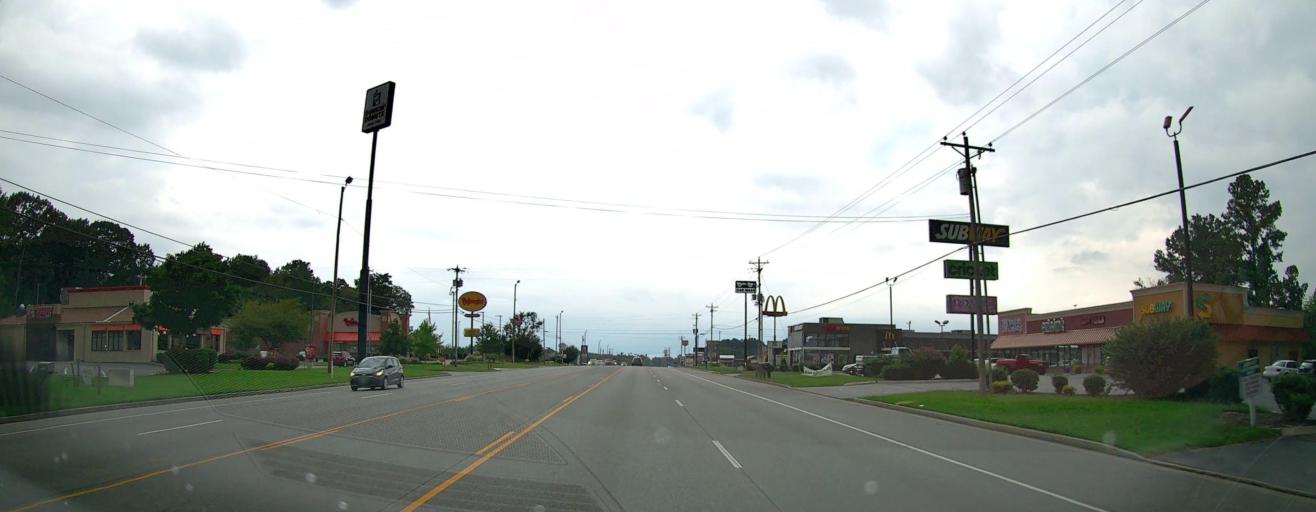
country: US
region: Tennessee
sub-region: Coffee County
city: Manchester
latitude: 35.4591
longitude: -86.0561
